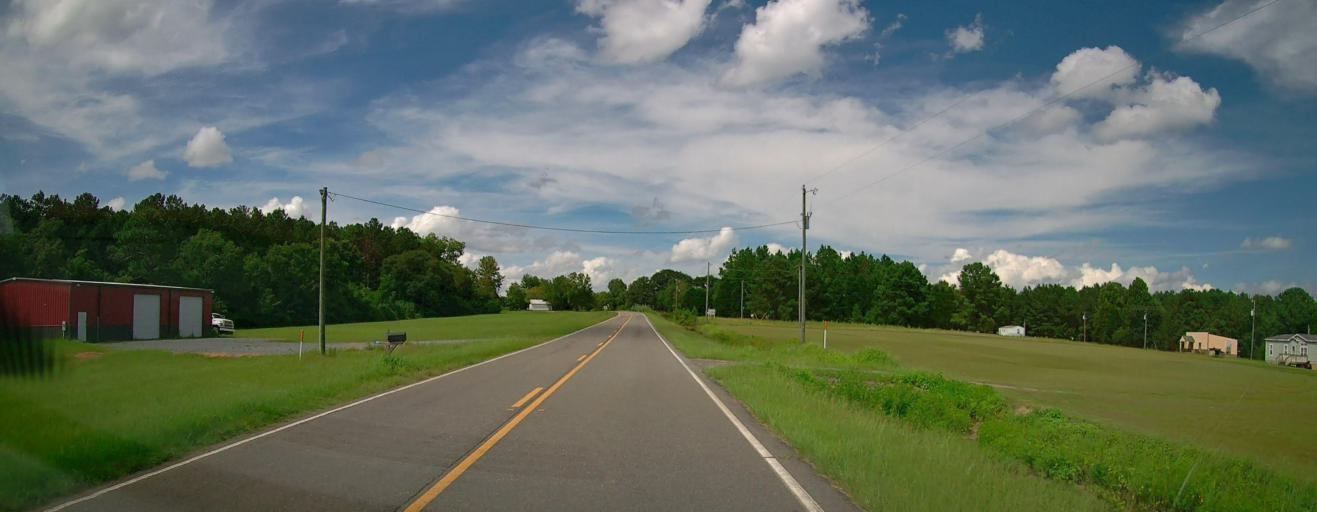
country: US
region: Georgia
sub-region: Taylor County
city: Butler
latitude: 32.4669
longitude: -84.1997
